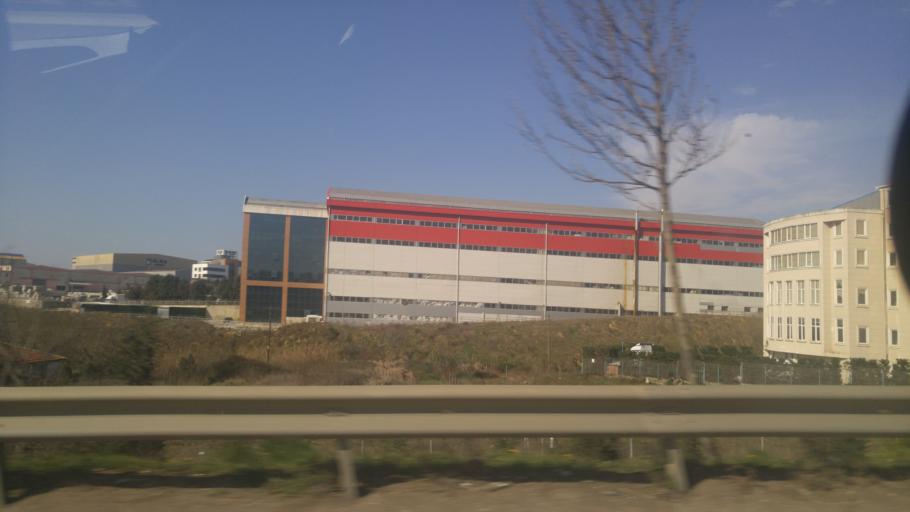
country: TR
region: Kocaeli
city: Balcik
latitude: 40.8523
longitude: 29.3747
